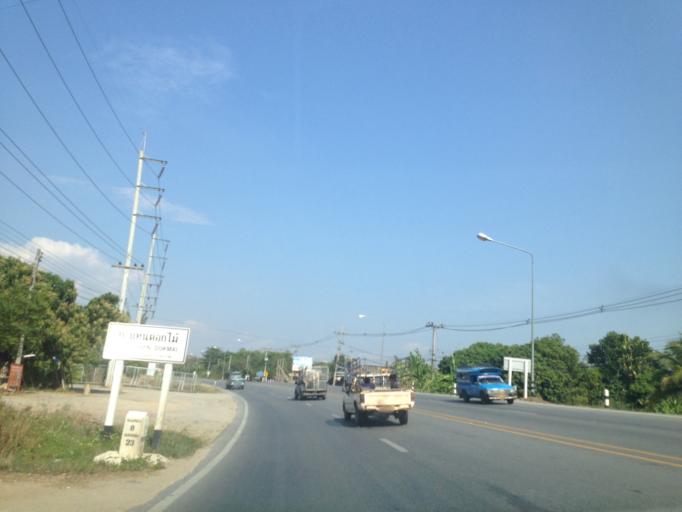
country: TH
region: Chiang Mai
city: Chom Thong
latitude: 18.3465
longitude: 98.6802
